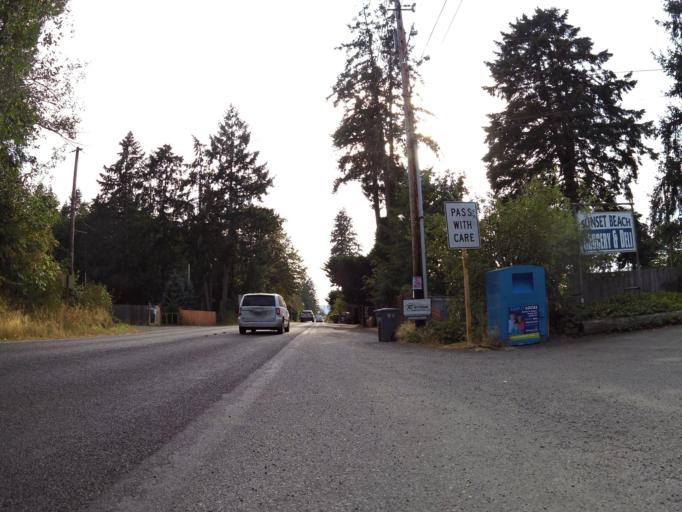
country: US
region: Washington
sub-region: Mason County
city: Allyn
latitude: 47.4071
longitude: -122.8860
